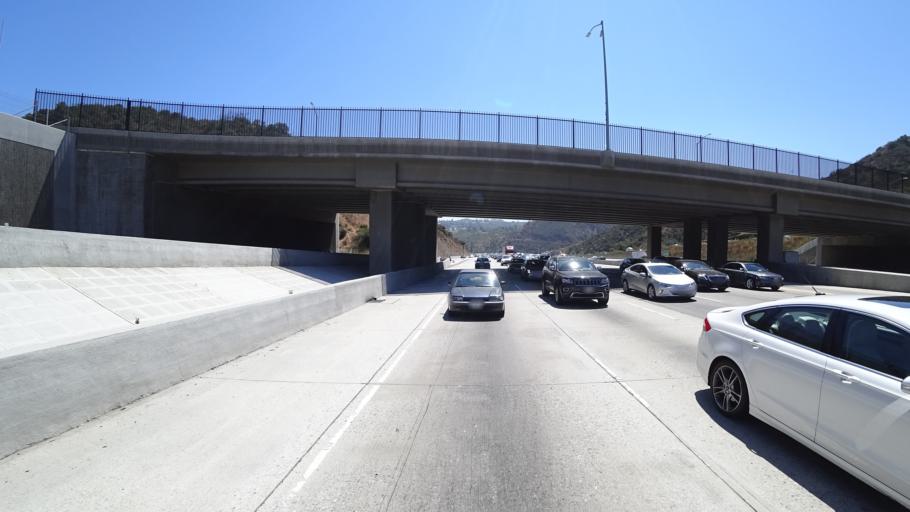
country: US
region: California
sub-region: Los Angeles County
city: Sherman Oaks
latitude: 34.1228
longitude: -118.4781
